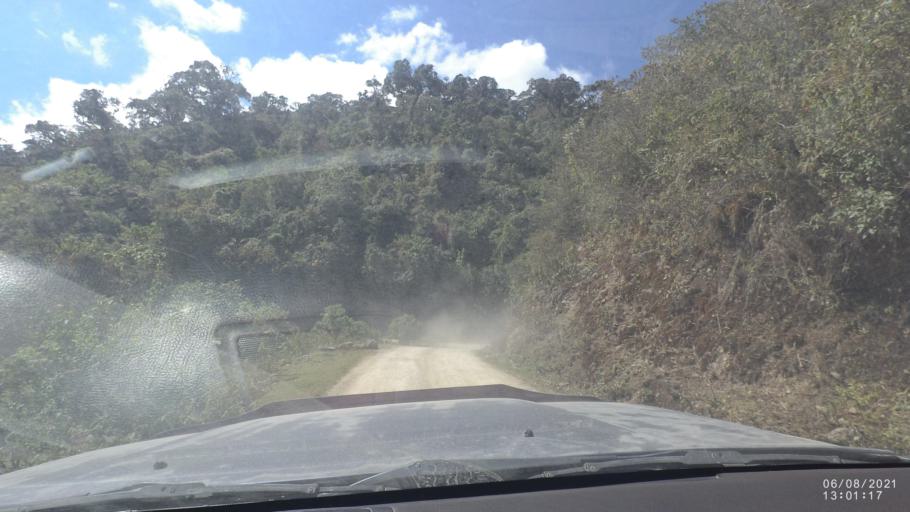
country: BO
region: Cochabamba
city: Colchani
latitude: -16.7443
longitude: -66.6913
